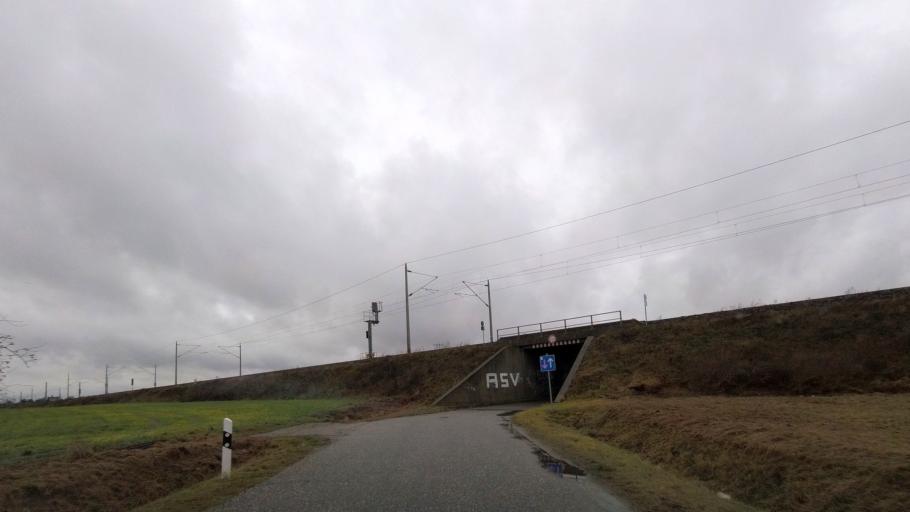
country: DE
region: Brandenburg
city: Niedergorsdorf
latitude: 51.9701
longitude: 12.9990
